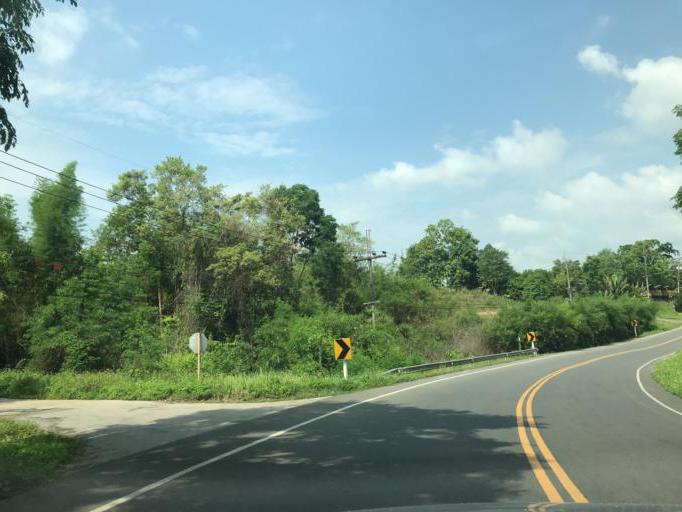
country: TH
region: Phayao
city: Pong
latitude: 19.1845
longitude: 100.2816
